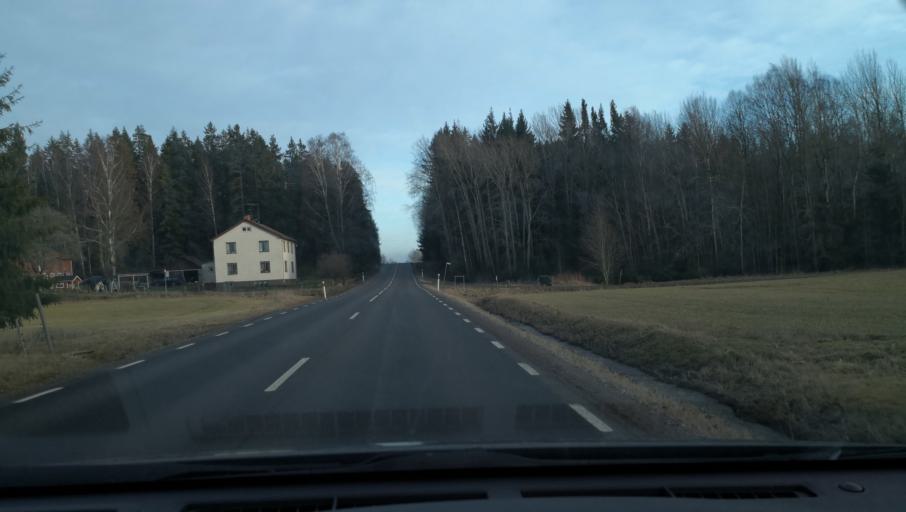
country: SE
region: Vaestra Goetaland
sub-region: Gullspangs Kommun
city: Gullspang
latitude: 59.0564
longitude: 14.2352
